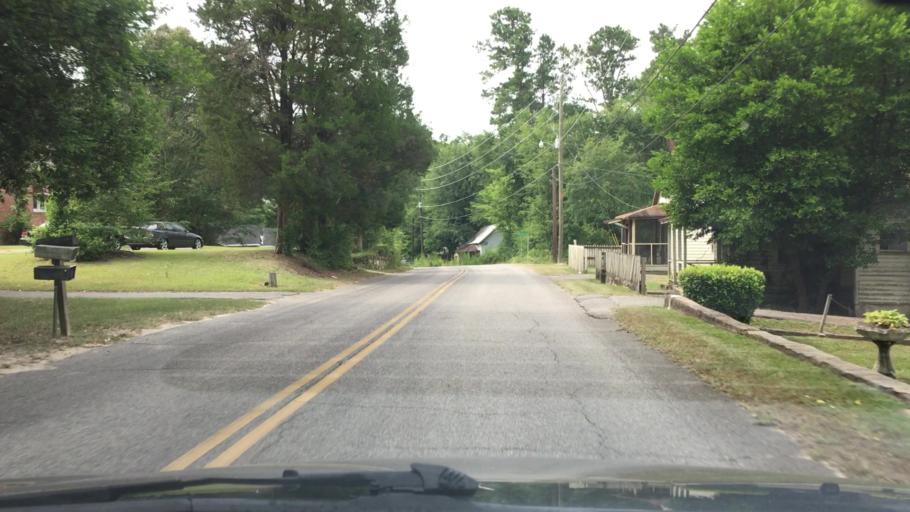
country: US
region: South Carolina
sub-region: Aiken County
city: Graniteville
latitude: 33.5591
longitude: -81.8032
